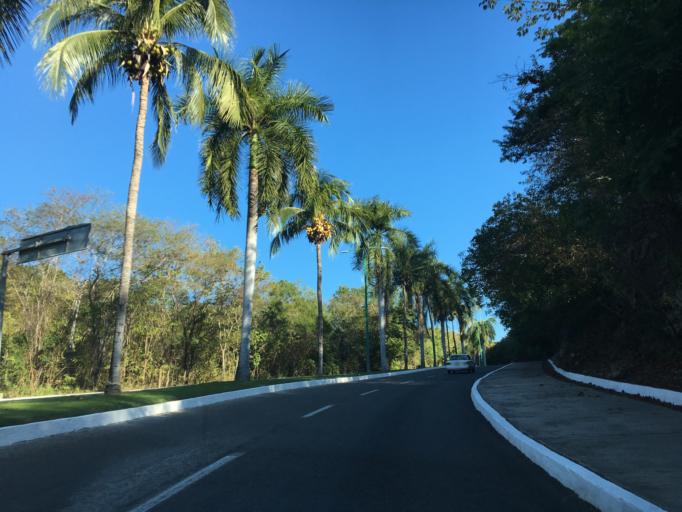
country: MX
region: Oaxaca
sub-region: Santa Maria Huatulco
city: Crucecita
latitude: 15.7667
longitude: -96.1138
